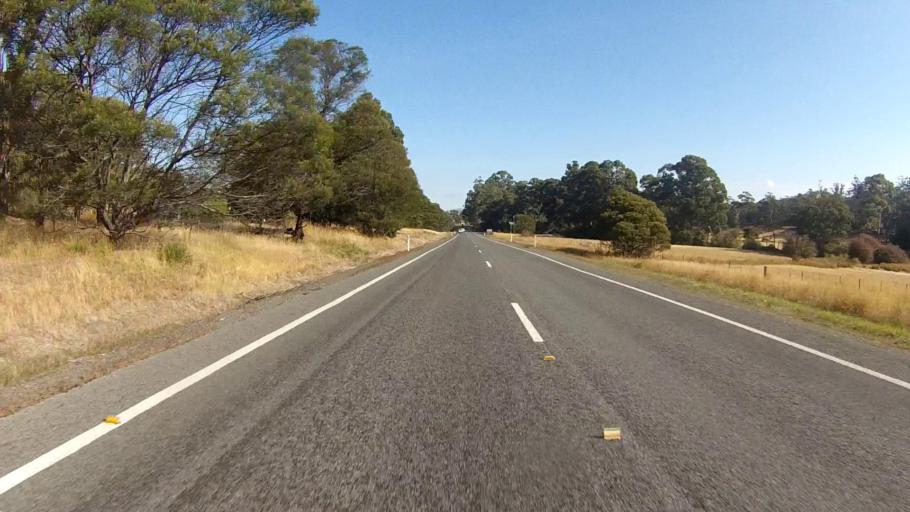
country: AU
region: Tasmania
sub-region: Sorell
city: Sorell
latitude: -42.6935
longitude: 147.5267
